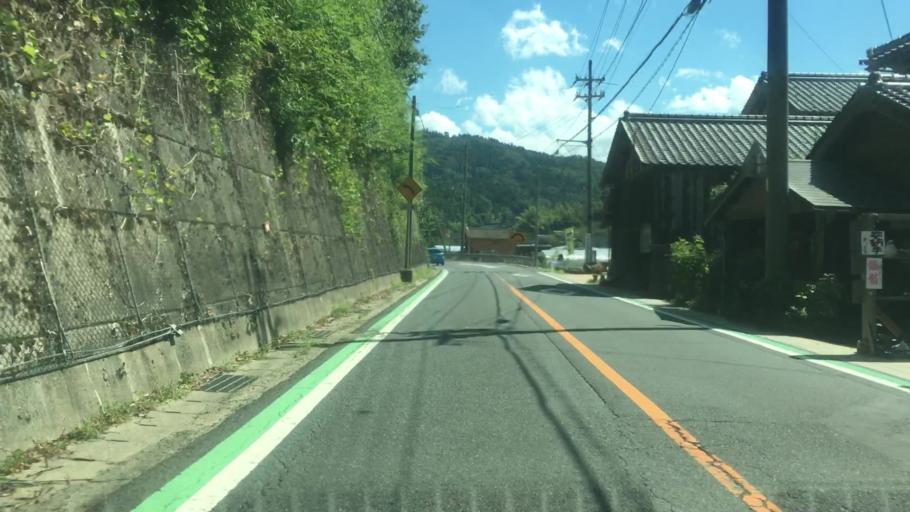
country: JP
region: Hyogo
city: Toyooka
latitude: 35.5951
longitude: 134.9056
